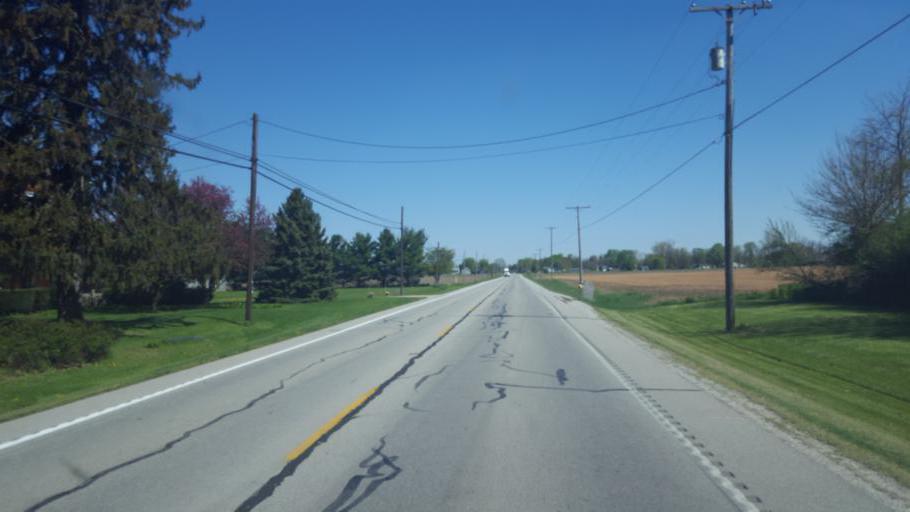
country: US
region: Ohio
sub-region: Seneca County
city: Tiffin
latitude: 41.1913
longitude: -83.1681
